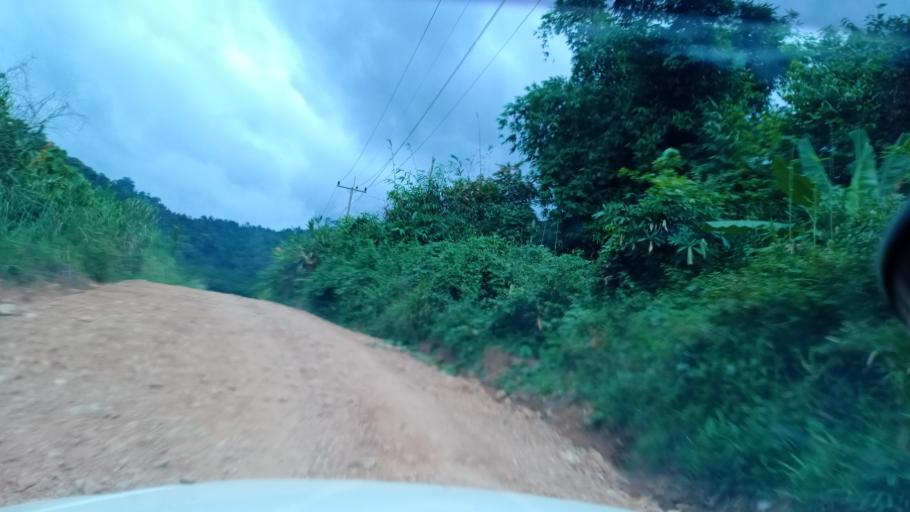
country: TH
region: Changwat Bueng Kan
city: Pak Khat
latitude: 18.7252
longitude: 103.2683
